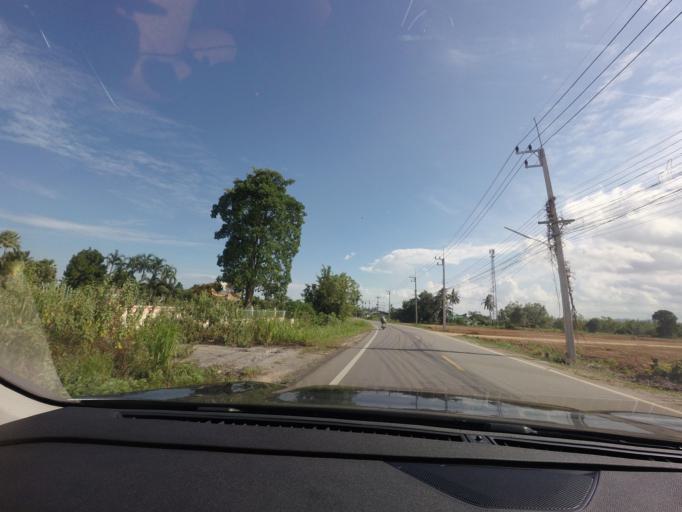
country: TH
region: Prachuap Khiri Khan
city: Pran Buri
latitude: 12.4357
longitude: 99.9445
